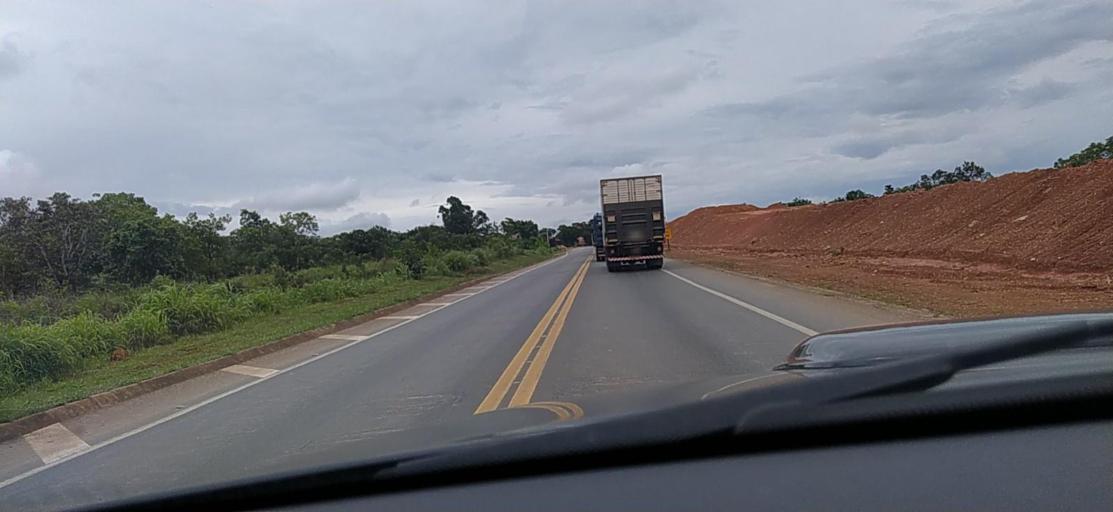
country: BR
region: Minas Gerais
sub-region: Curvelo
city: Curvelo
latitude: -18.7144
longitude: -44.4426
